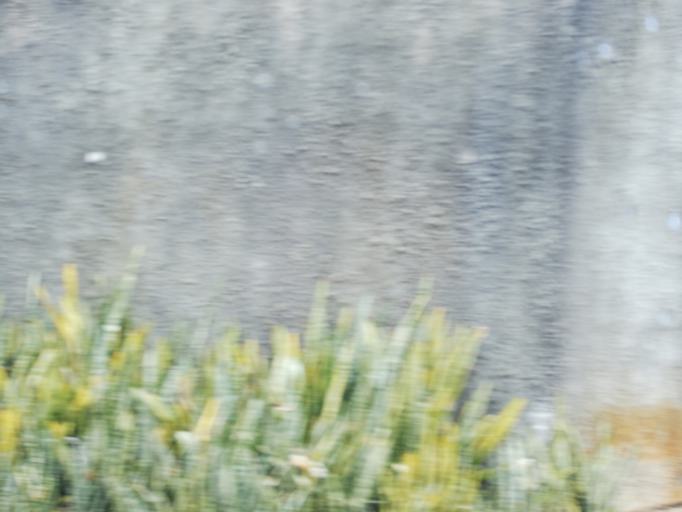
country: MU
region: Moka
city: Moka
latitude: -20.2160
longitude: 57.4744
